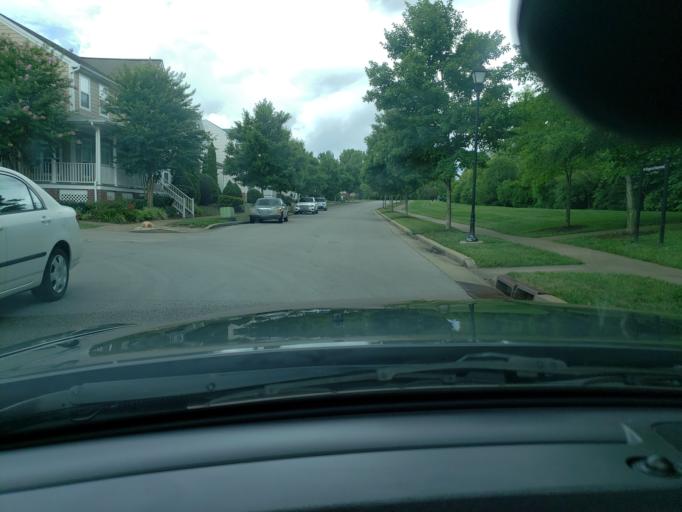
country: US
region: Tennessee
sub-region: Williamson County
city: Brentwood Estates
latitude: 36.0229
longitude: -86.7077
